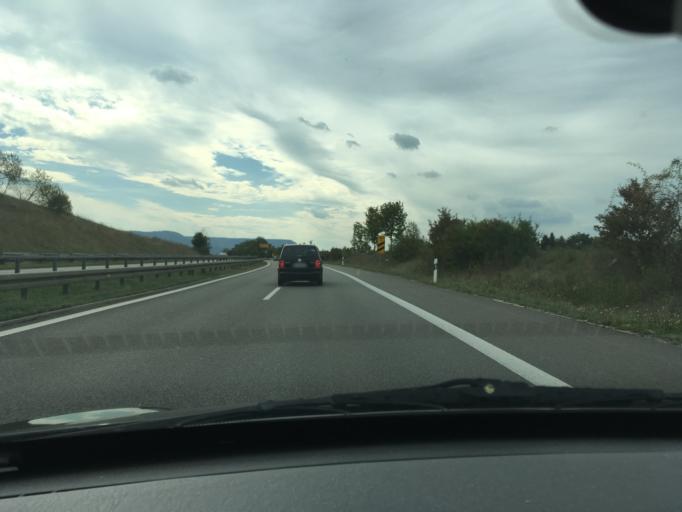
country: DE
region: Baden-Wuerttemberg
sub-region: Tuebingen Region
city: Dusslingen
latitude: 48.4633
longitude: 9.0618
